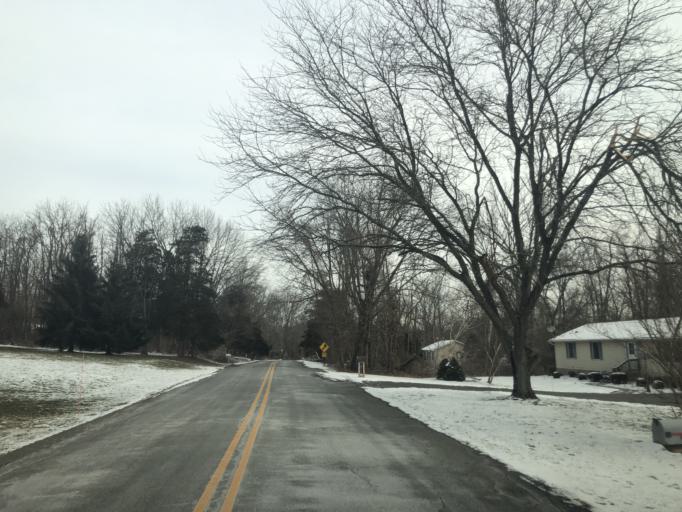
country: US
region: New Jersey
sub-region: Warren County
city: Belvidere
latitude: 40.9323
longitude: -75.0385
